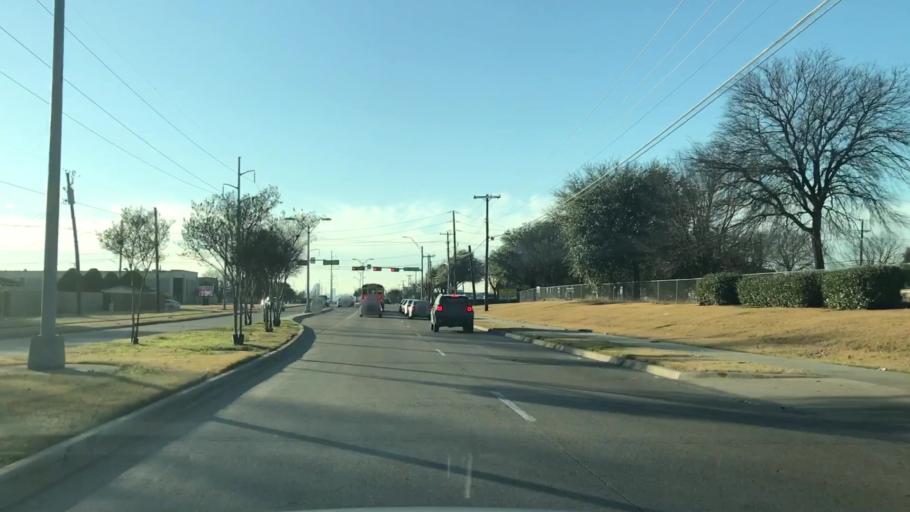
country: US
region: Texas
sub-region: Dallas County
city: Balch Springs
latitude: 32.7926
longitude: -96.6900
